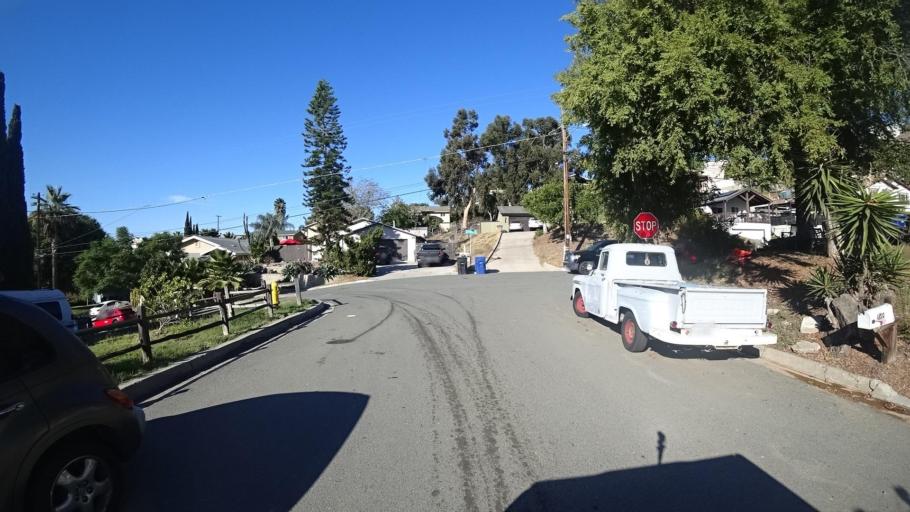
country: US
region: California
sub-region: San Diego County
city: La Presa
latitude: 32.7167
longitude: -116.9921
